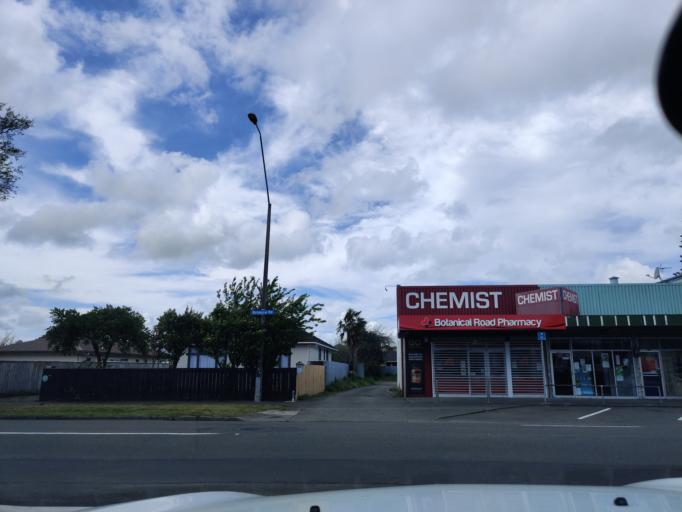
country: NZ
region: Manawatu-Wanganui
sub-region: Palmerston North City
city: Palmerston North
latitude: -40.3569
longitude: 175.5892
